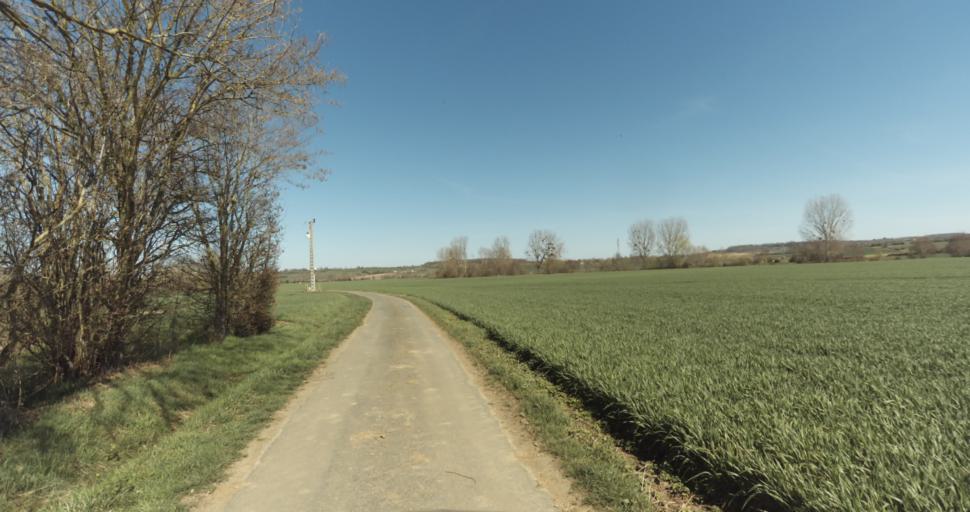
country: FR
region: Lower Normandy
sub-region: Departement du Calvados
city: Saint-Pierre-sur-Dives
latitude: 49.0259
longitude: 0.0198
